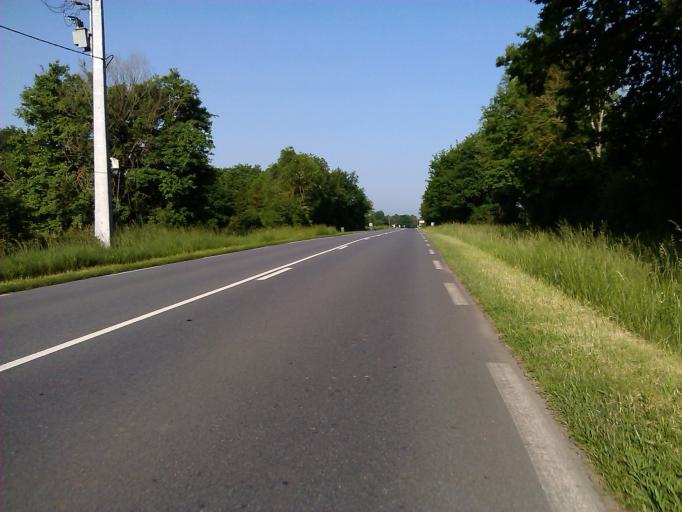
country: FR
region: Centre
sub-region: Departement de l'Indre
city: La Chatre
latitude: 46.5717
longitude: 1.9212
